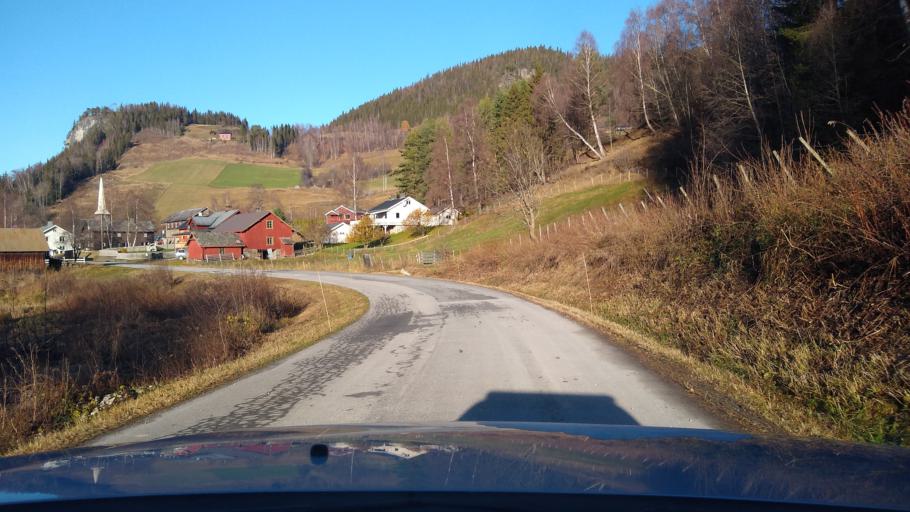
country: NO
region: Oppland
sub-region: Ringebu
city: Ringebu
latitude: 61.4251
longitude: 10.2233
